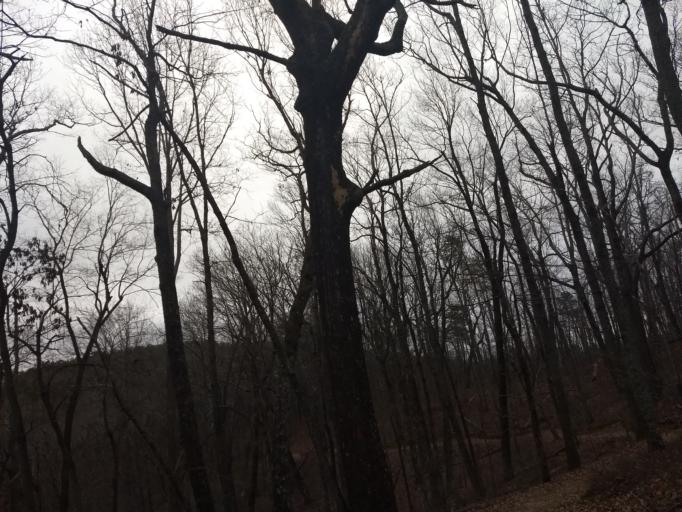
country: US
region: South Carolina
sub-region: Greenville County
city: Travelers Rest
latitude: 34.9445
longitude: -82.3990
